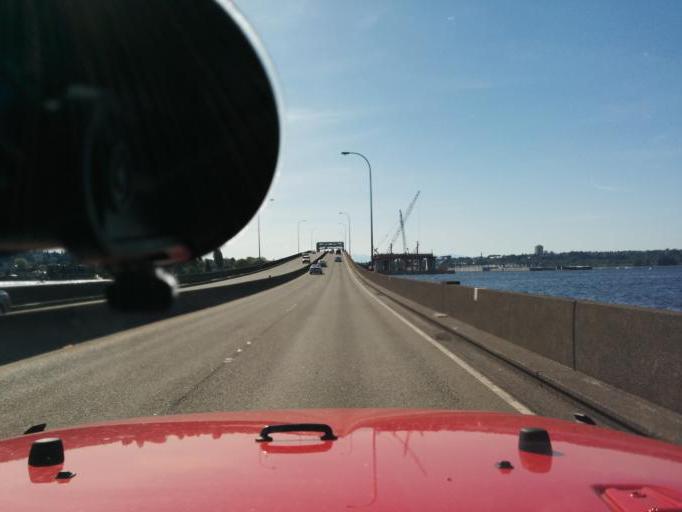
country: US
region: Washington
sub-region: King County
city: Medina
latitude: 47.6418
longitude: -122.2682
